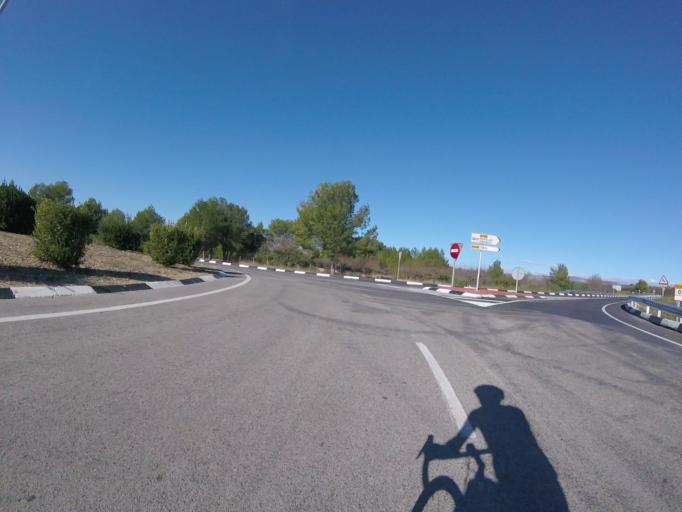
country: ES
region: Valencia
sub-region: Provincia de Castello
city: Chert/Xert
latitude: 40.4661
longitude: 0.1866
